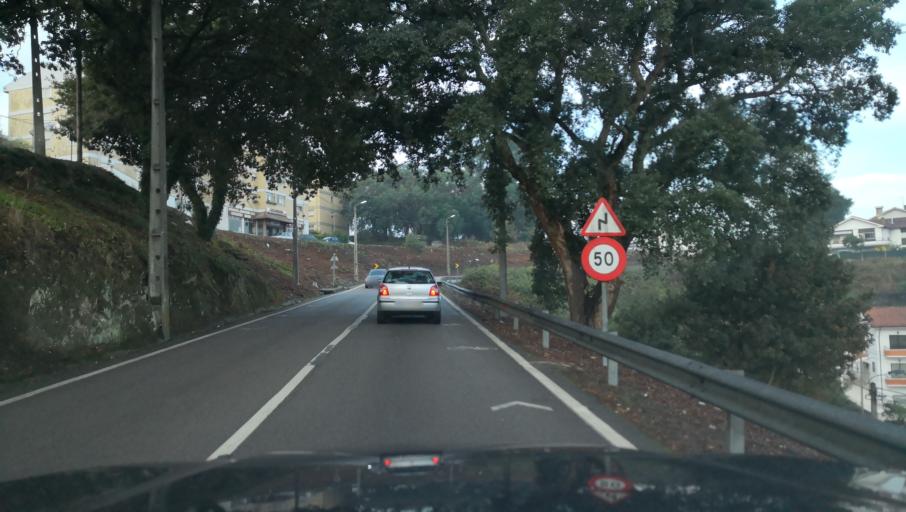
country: PT
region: Porto
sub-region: Gondomar
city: Valbom
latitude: 41.1446
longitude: -8.5623
